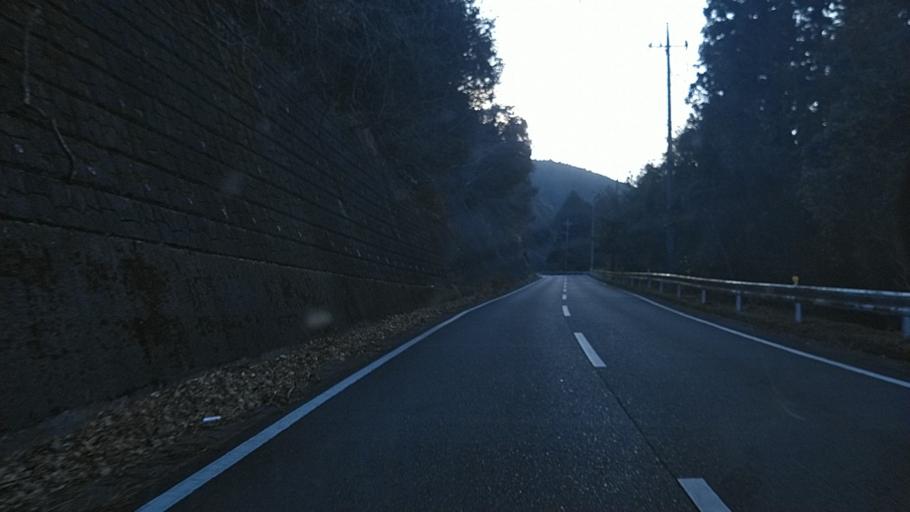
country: JP
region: Chiba
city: Kimitsu
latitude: 35.2659
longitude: 139.9290
